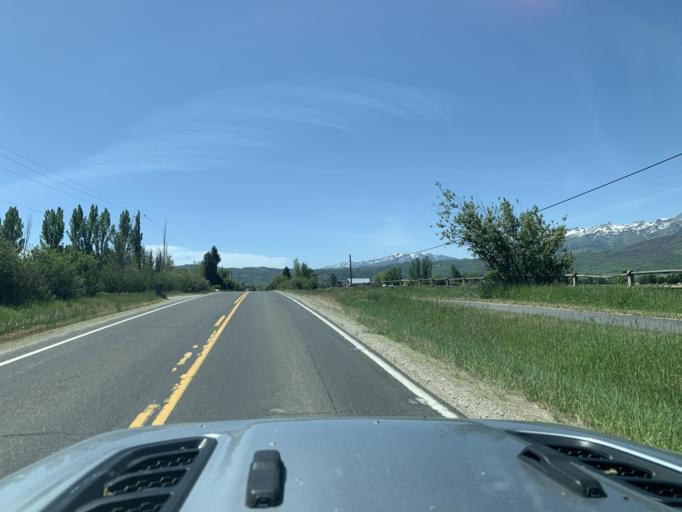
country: US
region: Utah
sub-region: Weber County
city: Wolf Creek
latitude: 41.2863
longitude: -111.7770
